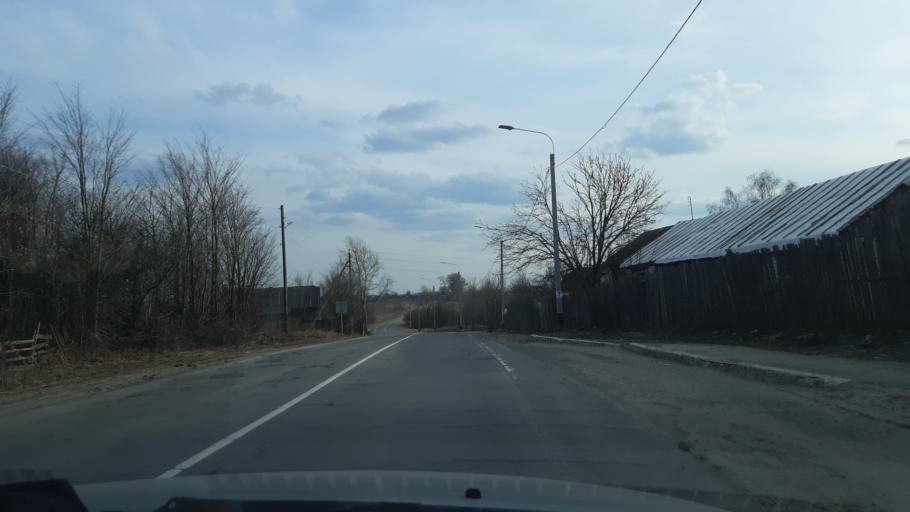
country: RU
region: Vladimir
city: Nikologory
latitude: 56.1610
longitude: 41.9955
